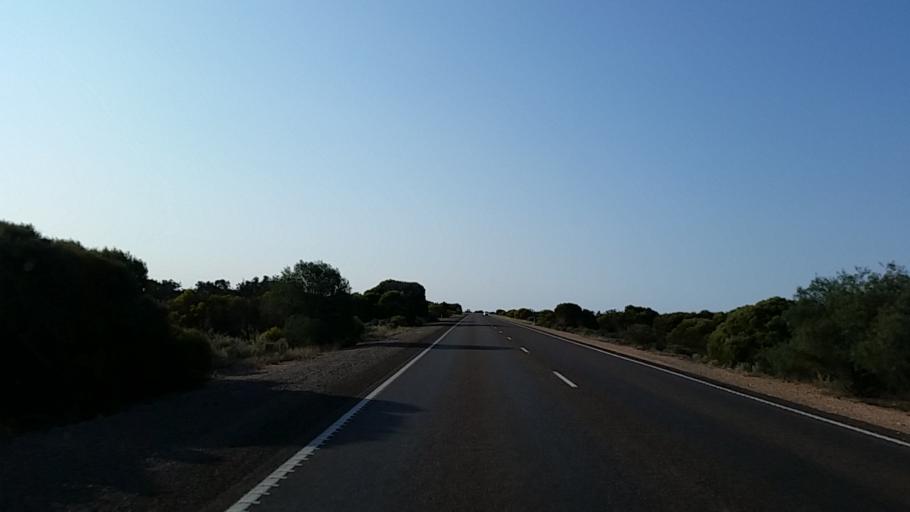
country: AU
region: South Australia
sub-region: Whyalla
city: Whyalla
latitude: -32.7920
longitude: 137.5372
